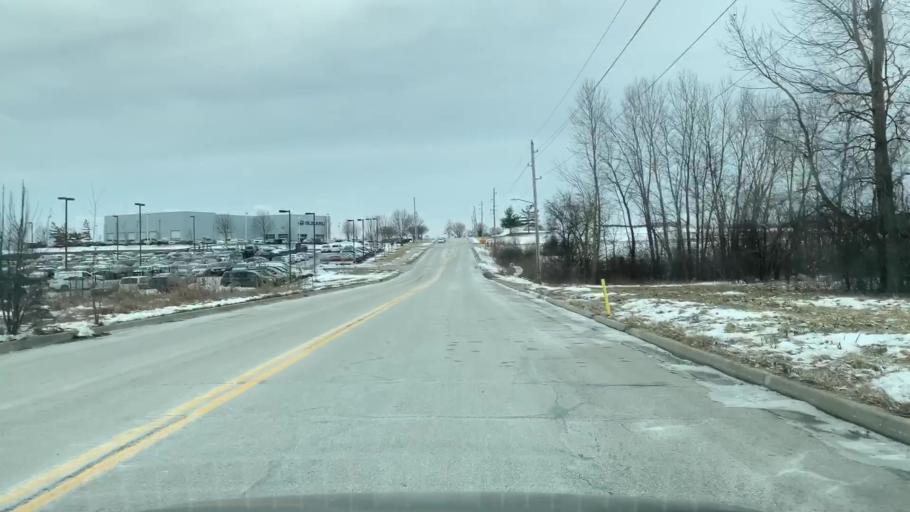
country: US
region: Missouri
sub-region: Jackson County
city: Lees Summit
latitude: 38.9516
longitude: -94.3641
